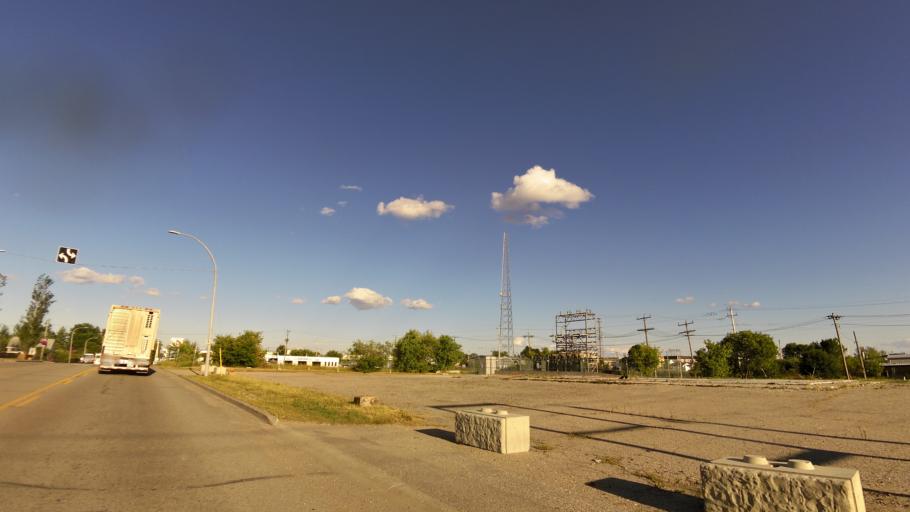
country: CA
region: Ontario
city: Dryden
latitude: 49.7867
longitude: -92.8430
